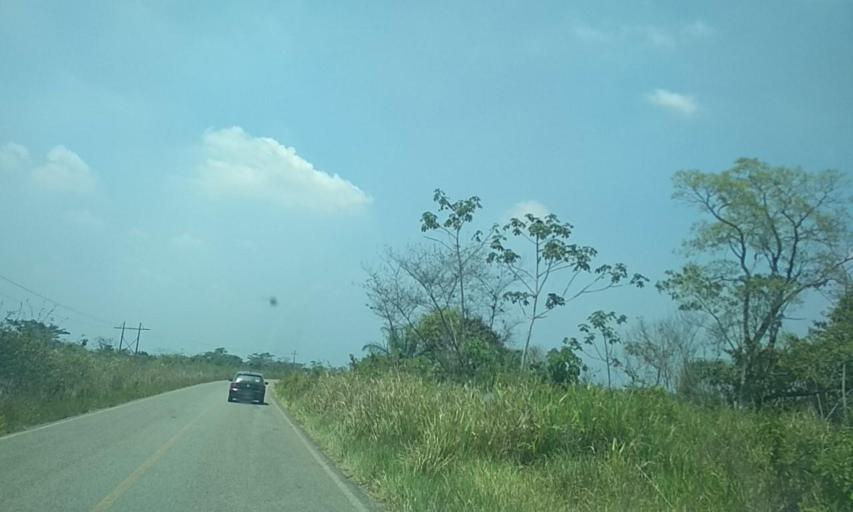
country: MX
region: Tabasco
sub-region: Huimanguillo
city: Paso de la Mina 3ra. Seccion
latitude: 17.8250
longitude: -93.6172
